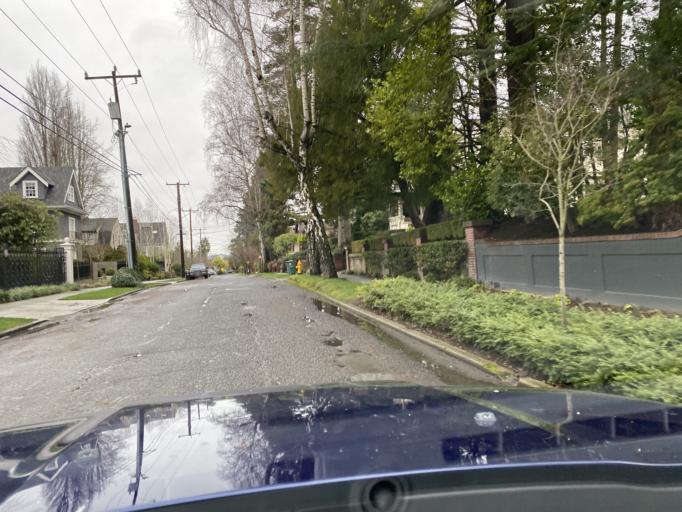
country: US
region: Washington
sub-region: King County
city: Seattle
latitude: 47.6337
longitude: -122.3191
